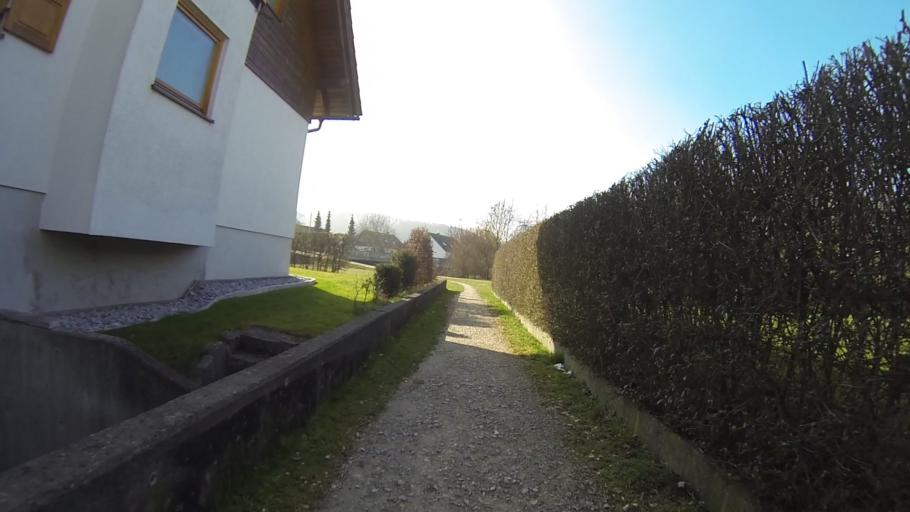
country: DE
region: Baden-Wuerttemberg
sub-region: Regierungsbezirk Stuttgart
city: Bolheim
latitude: 48.6332
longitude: 10.1553
